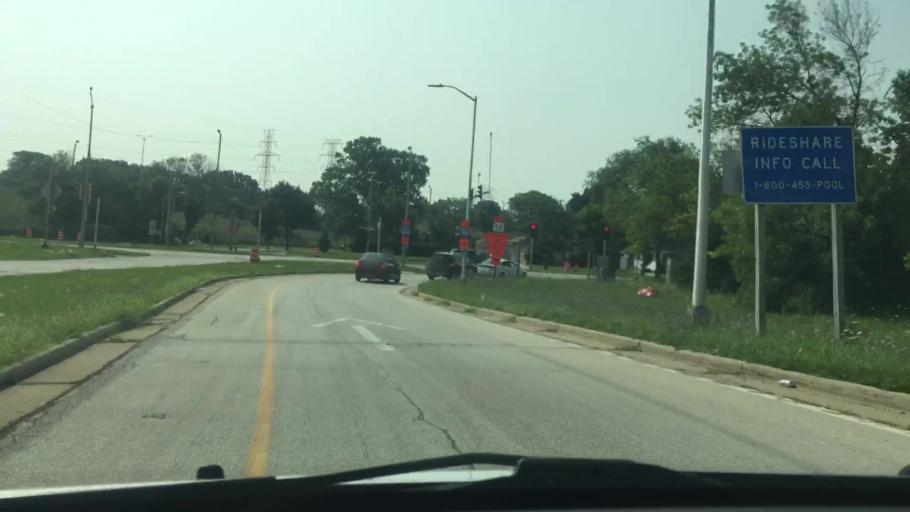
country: US
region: Wisconsin
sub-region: Milwaukee County
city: West Allis
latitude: 42.9988
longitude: -88.0397
